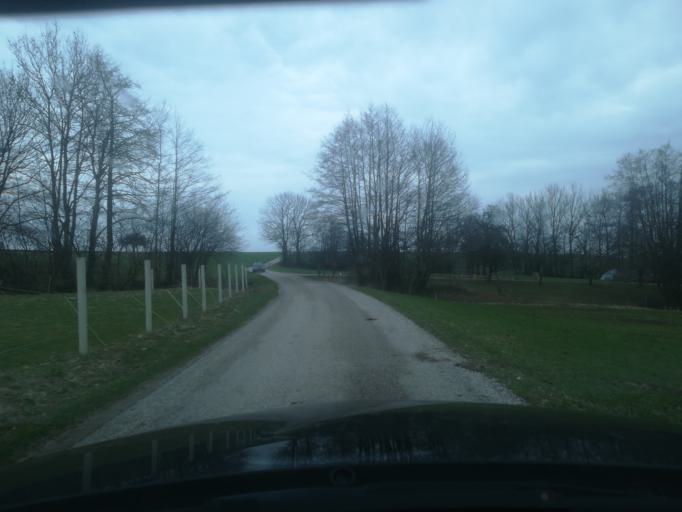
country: AT
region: Upper Austria
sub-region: Politischer Bezirk Rohrbach
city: Kleinzell im Muehlkreis
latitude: 48.3698
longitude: 13.9184
